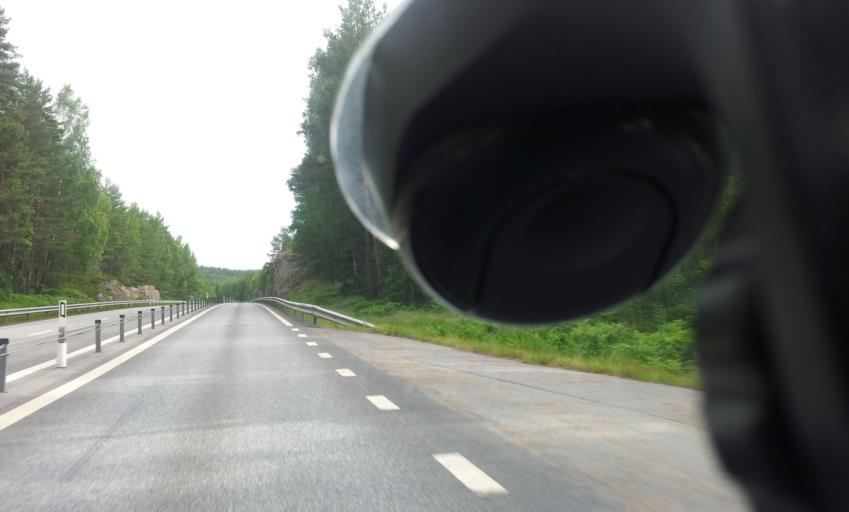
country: SE
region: OEstergoetland
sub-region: Valdemarsviks Kommun
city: Valdemarsvik
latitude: 58.1026
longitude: 16.5393
